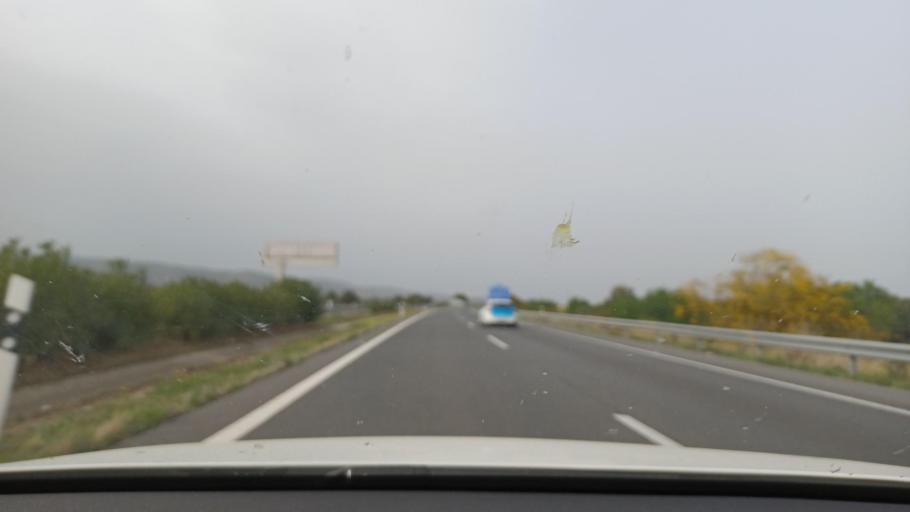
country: ES
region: Valencia
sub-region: Provincia de Castello
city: Orpesa/Oropesa del Mar
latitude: 40.1165
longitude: 0.1315
